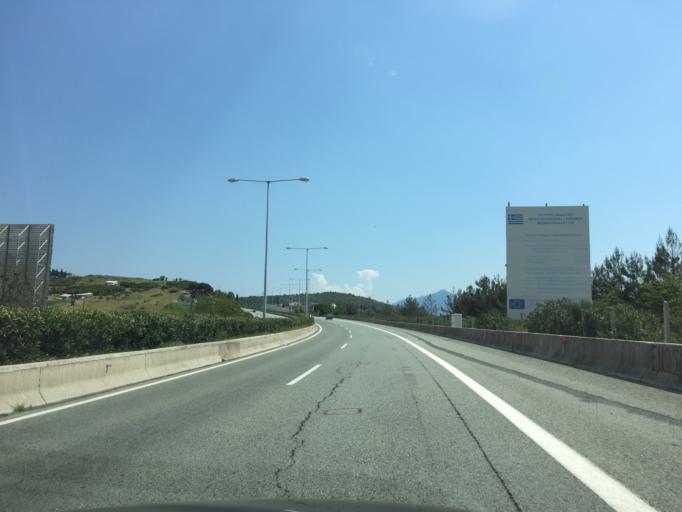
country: GR
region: Central Greece
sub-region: Nomos Fthiotidos
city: Pelasgia
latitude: 38.8846
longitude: 22.7686
